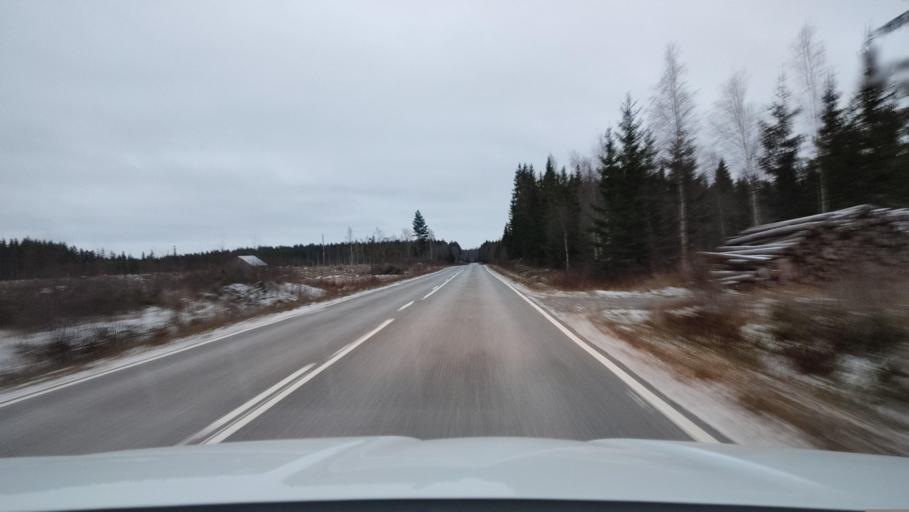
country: FI
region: Ostrobothnia
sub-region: Vaasa
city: Replot
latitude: 63.2452
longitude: 21.3801
